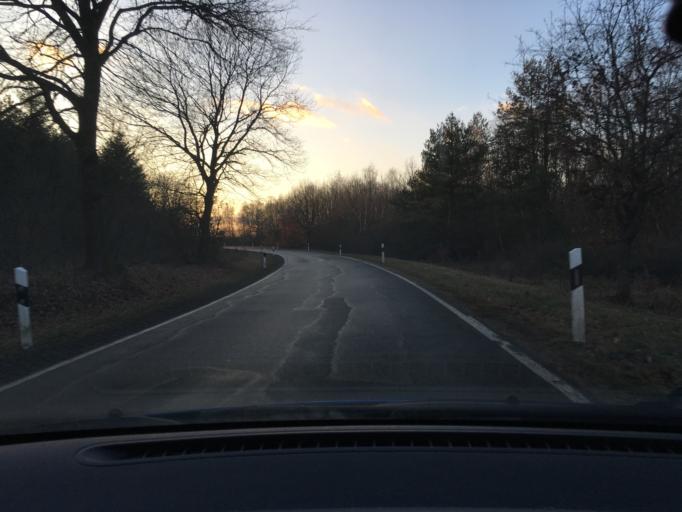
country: DE
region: Schleswig-Holstein
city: Brothen
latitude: 53.4854
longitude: 10.6765
